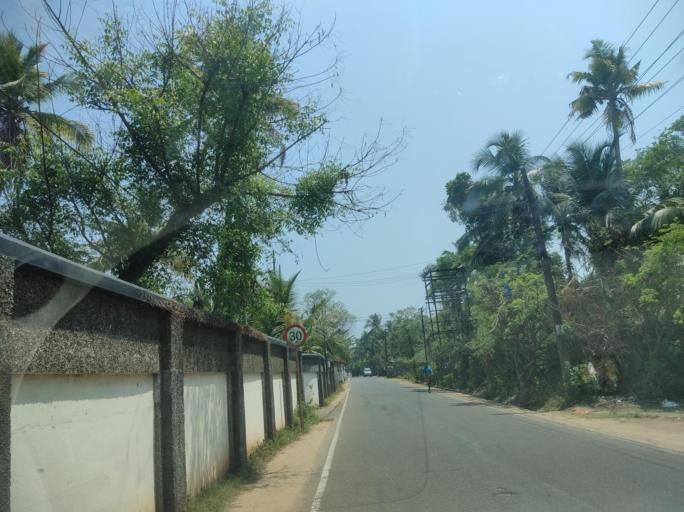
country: IN
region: Kerala
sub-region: Alappuzha
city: Kutiatodu
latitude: 9.8202
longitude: 76.2988
